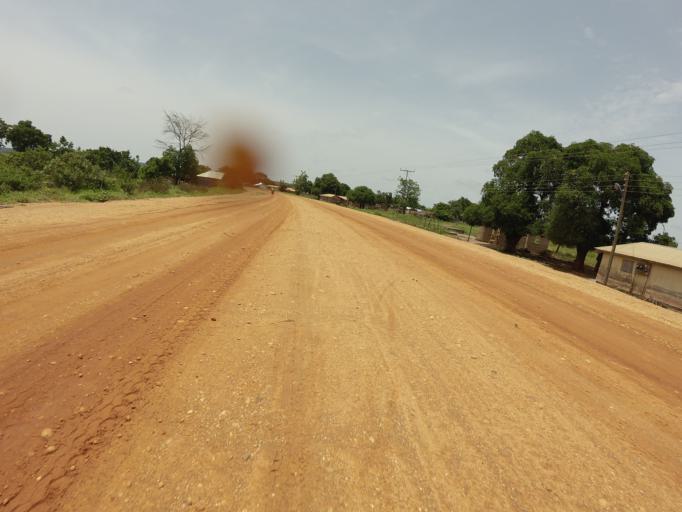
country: GH
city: Kpandae
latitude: 8.7055
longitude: 0.1602
